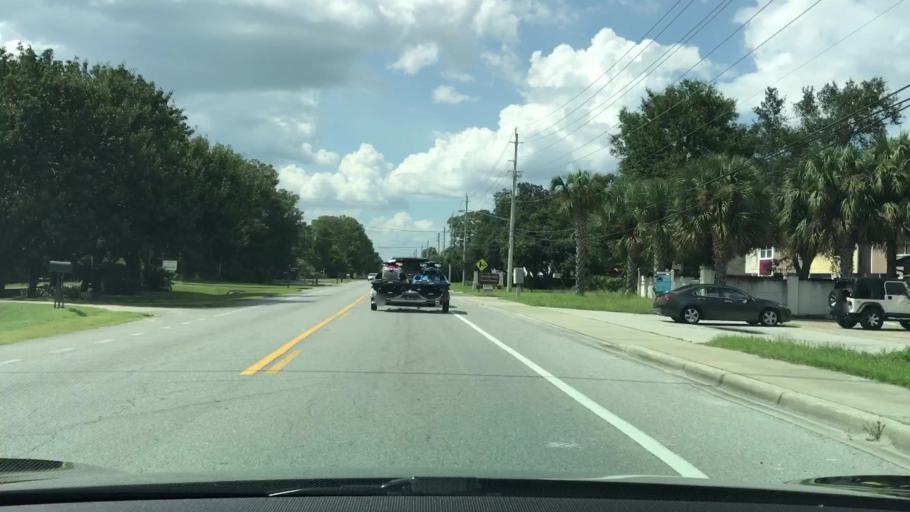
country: US
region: Florida
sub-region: Bay County
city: Lower Grand Lagoon
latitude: 30.1564
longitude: -85.7567
